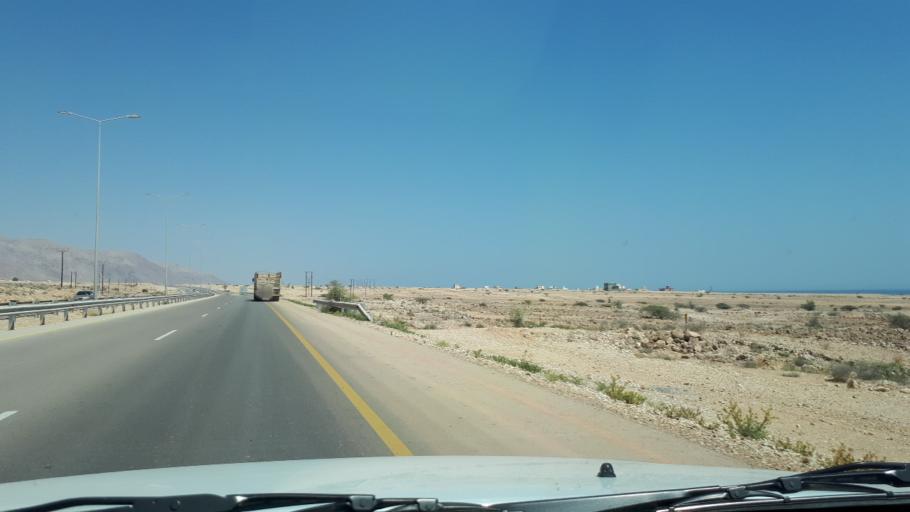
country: OM
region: Ash Sharqiyah
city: Sur
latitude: 22.7346
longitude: 59.3389
